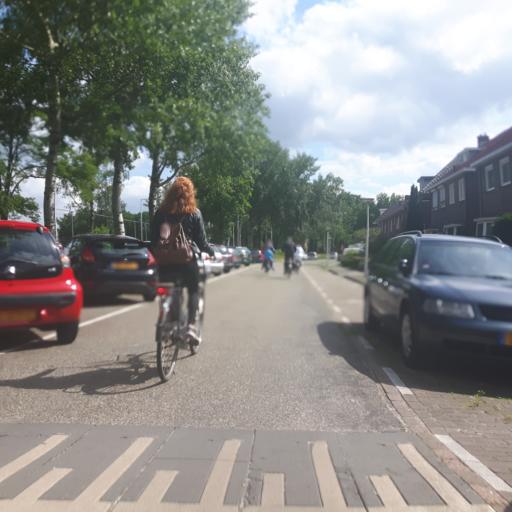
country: NL
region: Overijssel
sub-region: Gemeente Enschede
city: Enschede
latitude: 52.2056
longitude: 6.8955
